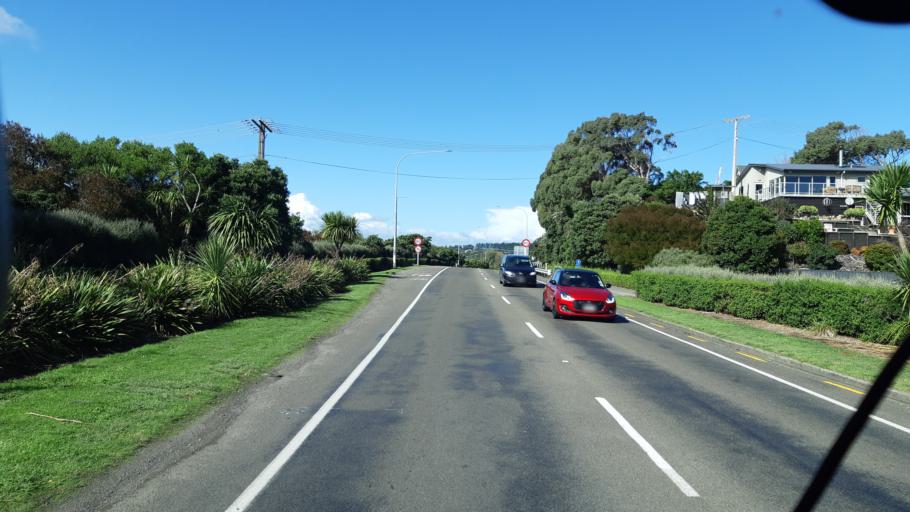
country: NZ
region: Manawatu-Wanganui
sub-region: Wanganui District
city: Wanganui
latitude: -39.9419
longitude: 175.0427
